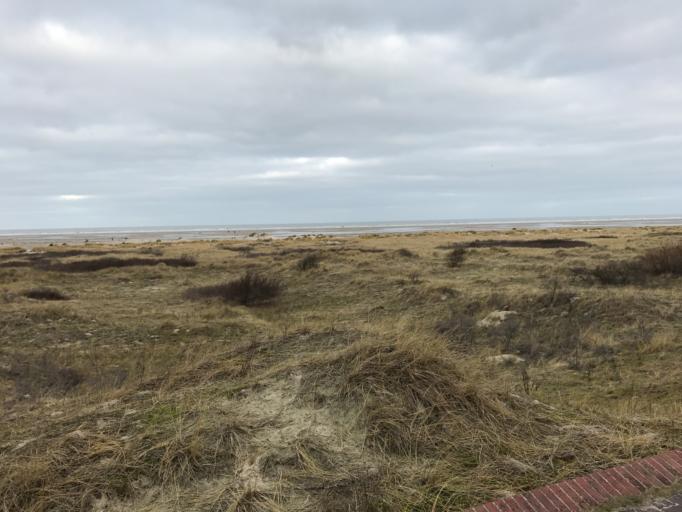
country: DE
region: Lower Saxony
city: Borkum
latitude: 53.6010
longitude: 6.6772
